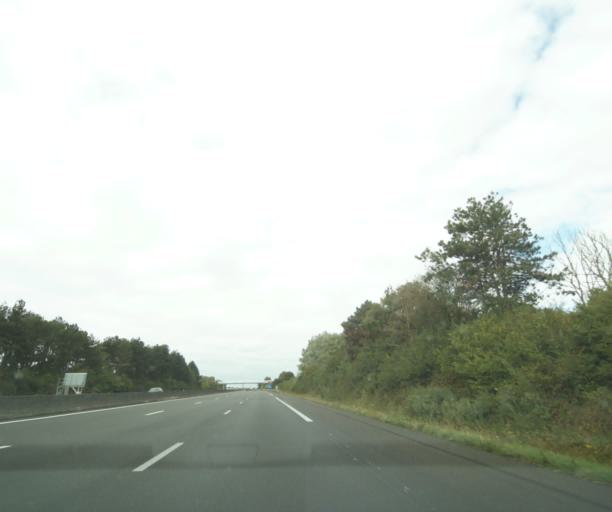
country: FR
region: Centre
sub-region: Departement d'Eure-et-Loir
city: Janville
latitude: 48.2373
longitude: 1.8505
